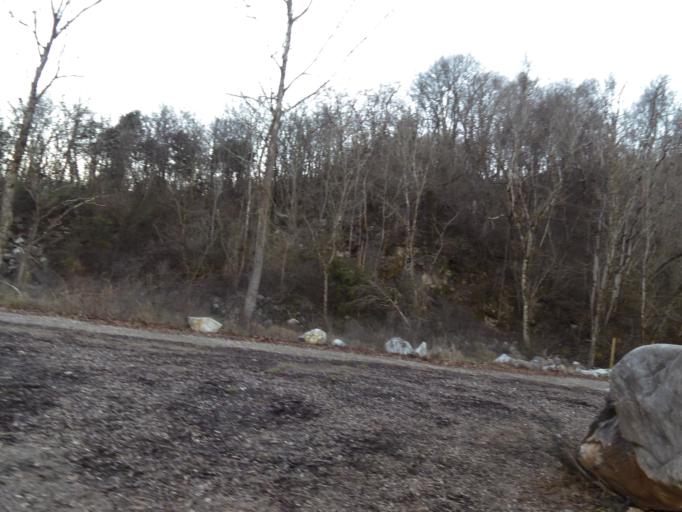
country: US
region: Tennessee
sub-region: Knox County
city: Knoxville
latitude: 35.9550
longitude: -83.8621
